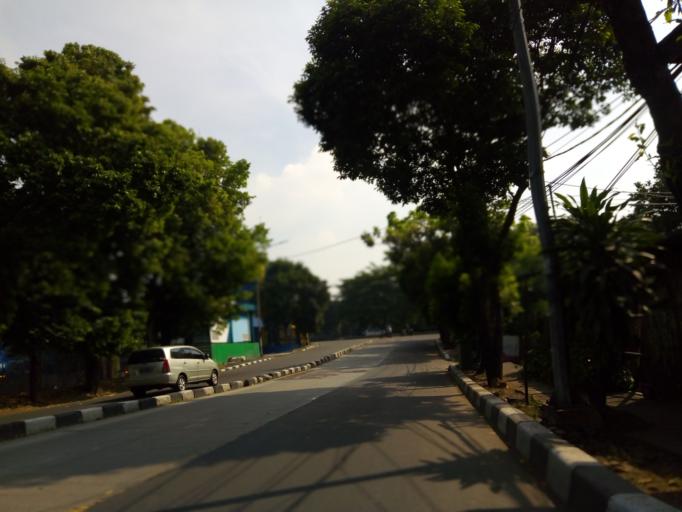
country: ID
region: Jakarta Raya
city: Jakarta
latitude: -6.2055
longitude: 106.8301
